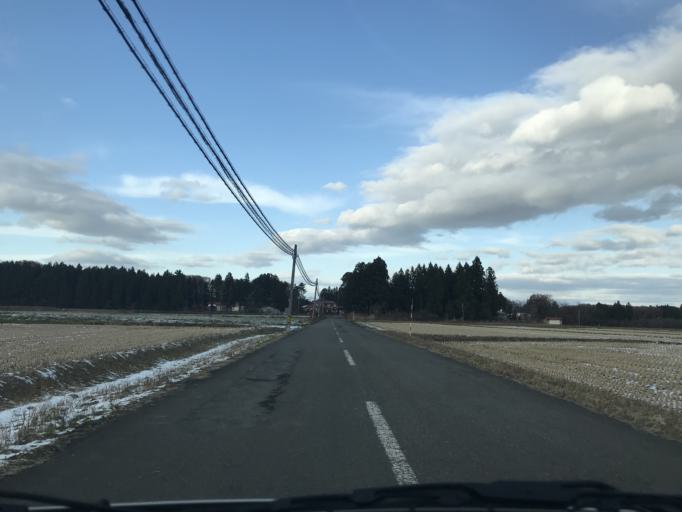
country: JP
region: Iwate
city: Kitakami
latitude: 39.2233
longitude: 141.0441
